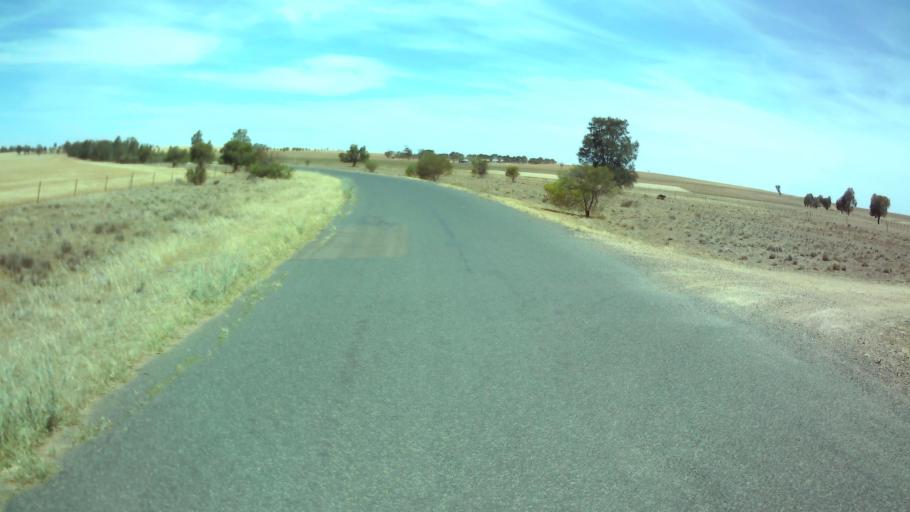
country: AU
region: New South Wales
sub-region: Weddin
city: Grenfell
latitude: -33.8890
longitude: 147.7420
